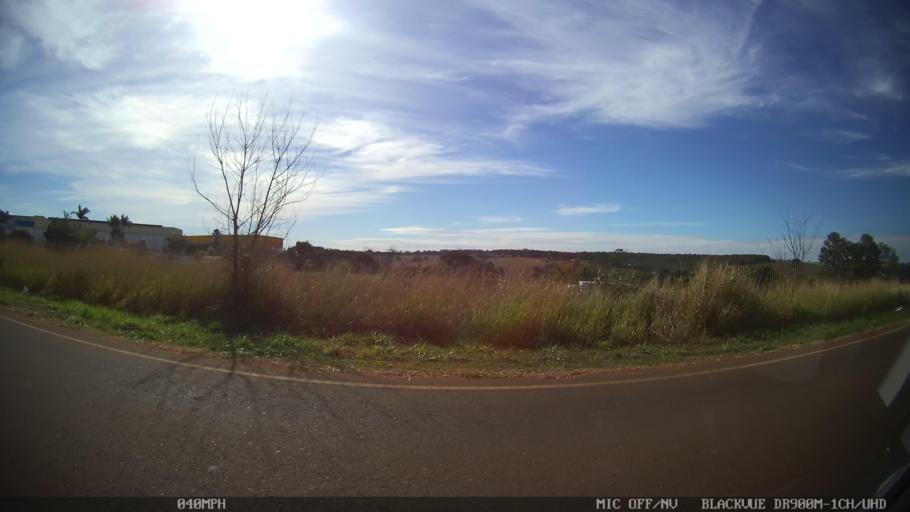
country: BR
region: Sao Paulo
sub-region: Sao Jose Do Rio Preto
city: Sao Jose do Rio Preto
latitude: -20.7982
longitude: -49.3258
